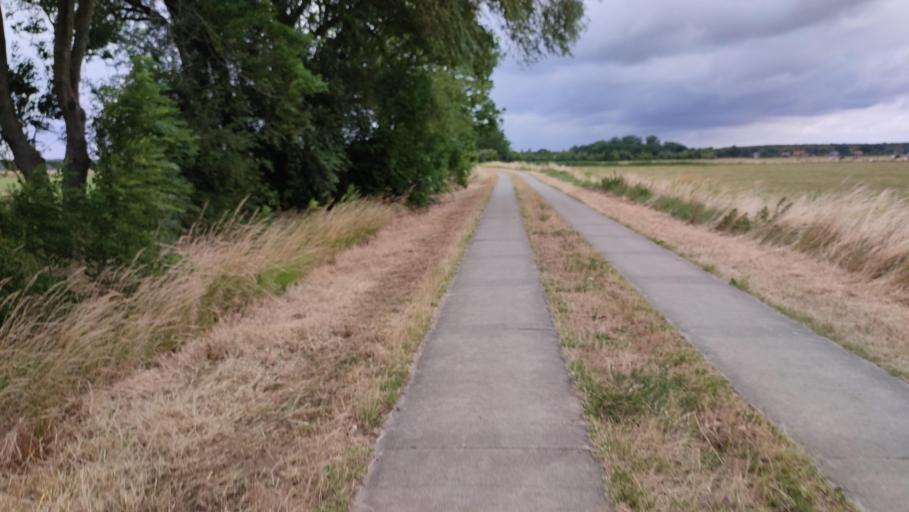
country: DE
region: Lower Saxony
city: Hitzacker
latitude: 53.1706
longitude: 11.1024
